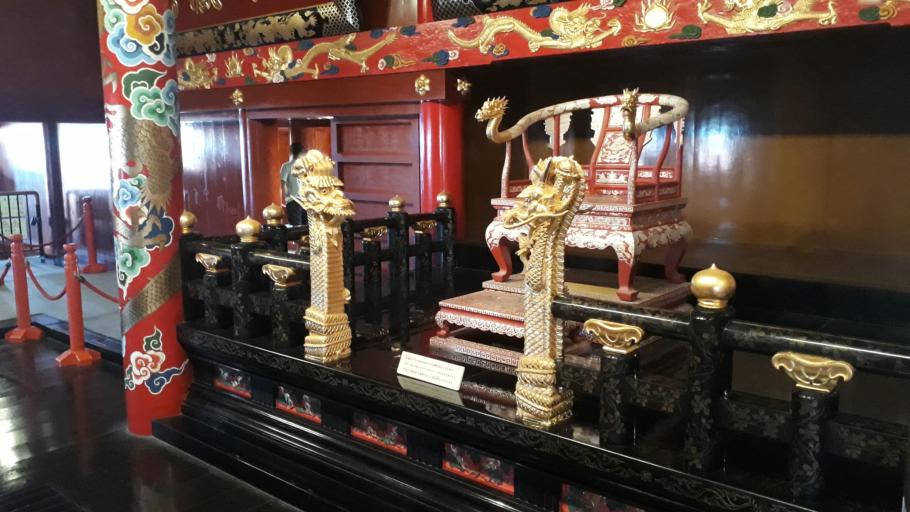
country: JP
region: Okinawa
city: Naha-shi
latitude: 26.2175
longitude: 127.7231
